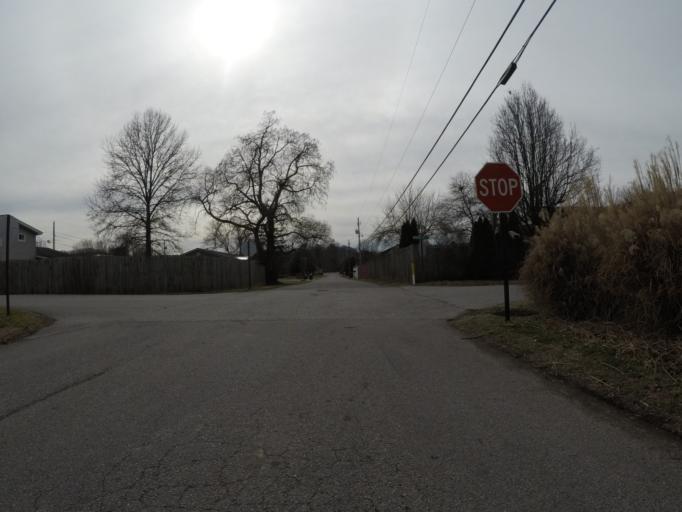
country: US
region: West Virginia
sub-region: Cabell County
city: Pea Ridge
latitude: 38.4525
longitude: -82.3413
